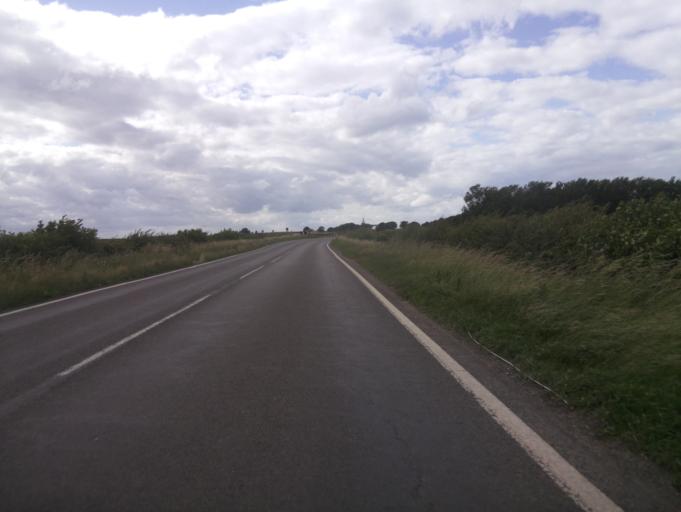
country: GB
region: England
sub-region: Leicestershire
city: Measham
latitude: 52.6569
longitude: -1.5366
